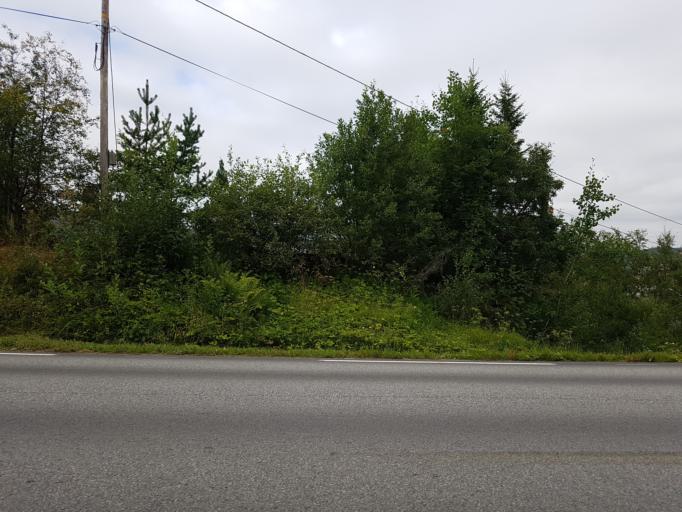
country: NO
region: Sor-Trondelag
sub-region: Agdenes
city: Lensvik
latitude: 63.6345
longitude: 9.8350
